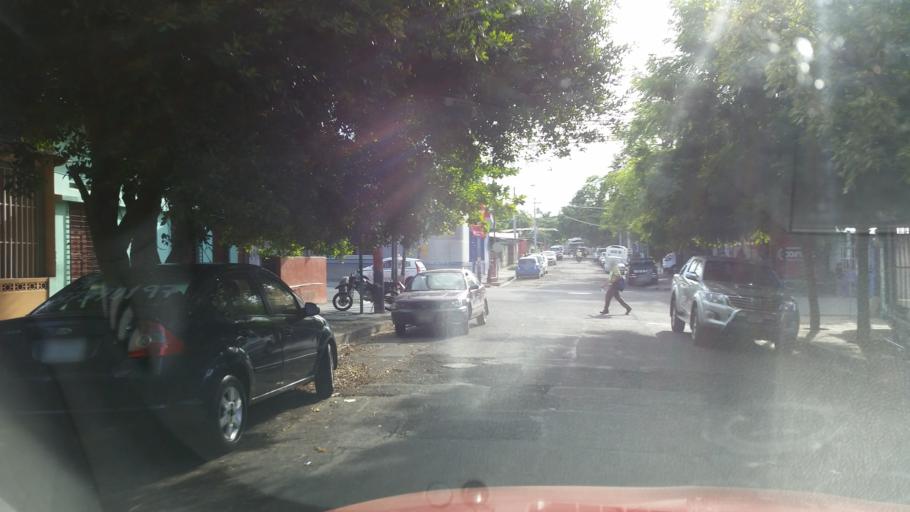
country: NI
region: Managua
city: Managua
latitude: 12.1448
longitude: -86.2822
